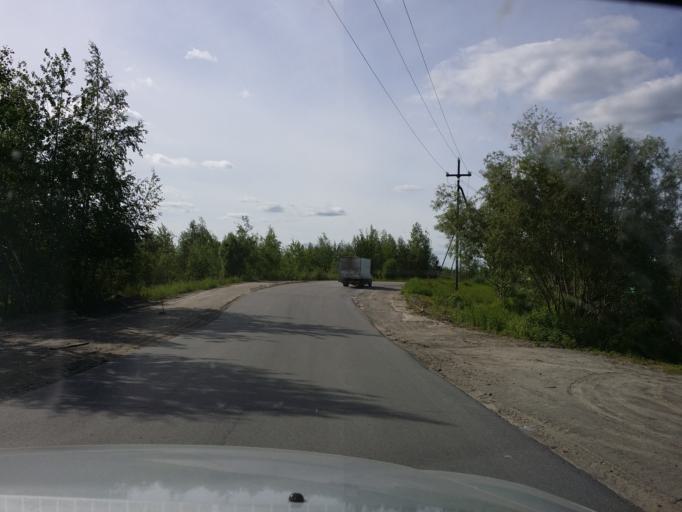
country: RU
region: Khanty-Mansiyskiy Avtonomnyy Okrug
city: Nizhnevartovsk
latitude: 61.0015
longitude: 76.5603
